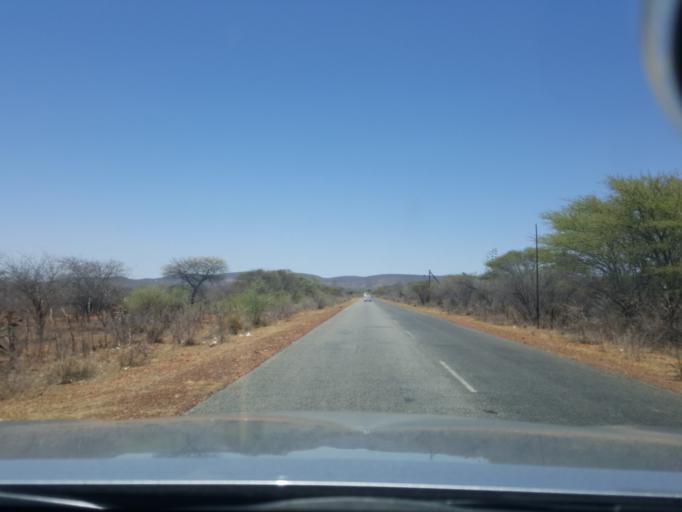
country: BW
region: South East
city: Lobatse
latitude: -25.2413
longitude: 25.9340
